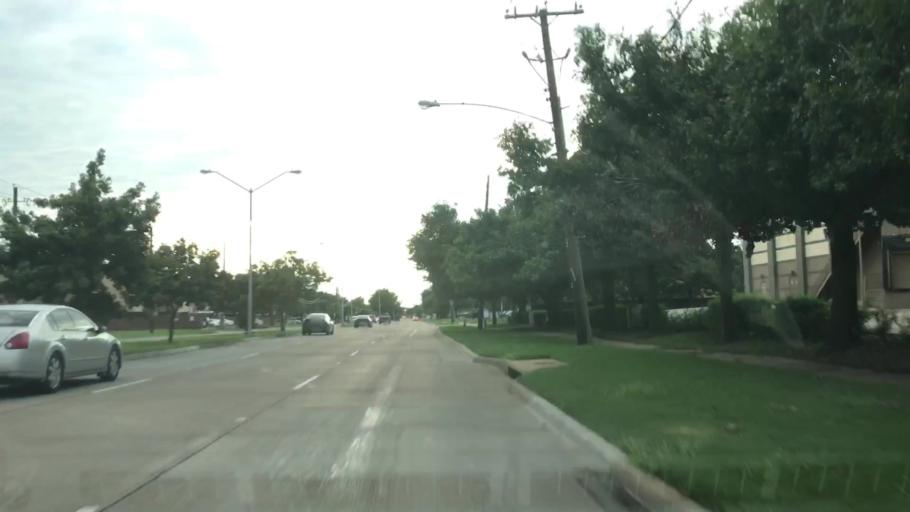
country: US
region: Texas
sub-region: Dallas County
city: Farmers Branch
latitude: 32.9099
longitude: -96.8743
